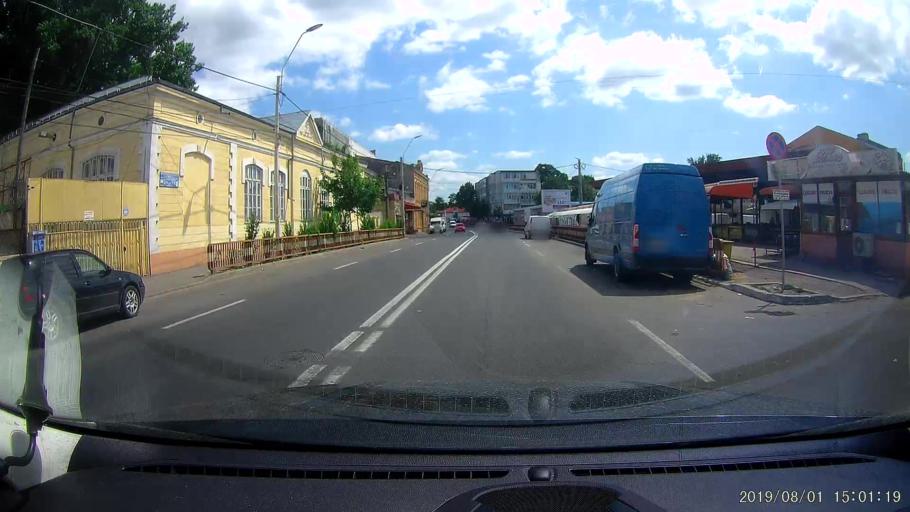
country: RO
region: Braila
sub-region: Municipiul Braila
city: Braila
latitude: 45.2725
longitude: 27.9604
